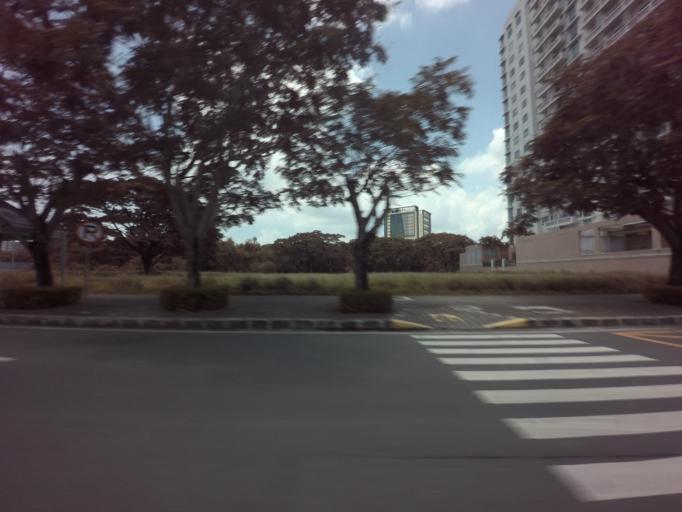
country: PH
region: Calabarzon
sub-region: Province of Laguna
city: San Pedro
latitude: 14.4141
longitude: 121.0367
